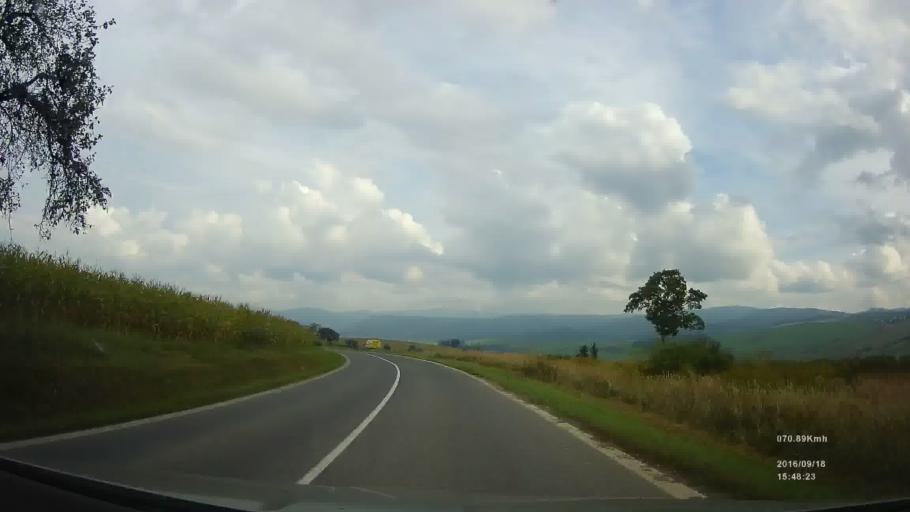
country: SK
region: Kosicky
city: Spisska Nova Ves
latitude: 48.9267
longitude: 20.5941
